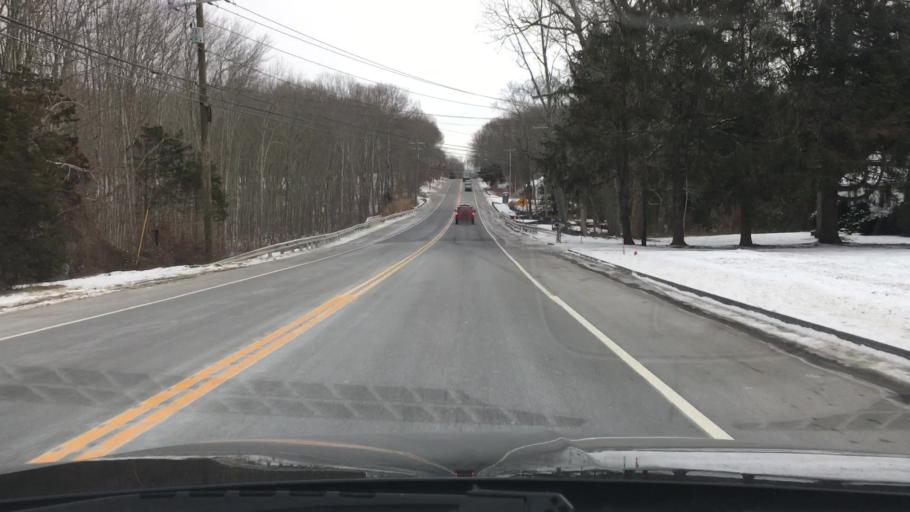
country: US
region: Connecticut
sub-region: New London County
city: Ledyard Center
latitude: 41.4922
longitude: -72.0134
